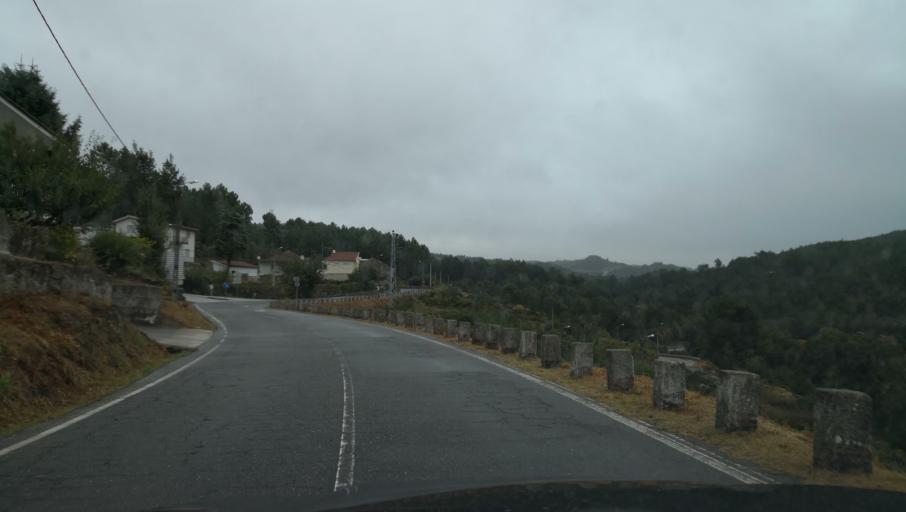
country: PT
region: Vila Real
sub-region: Sabrosa
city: Sabrosa
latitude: 41.3520
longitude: -7.5890
